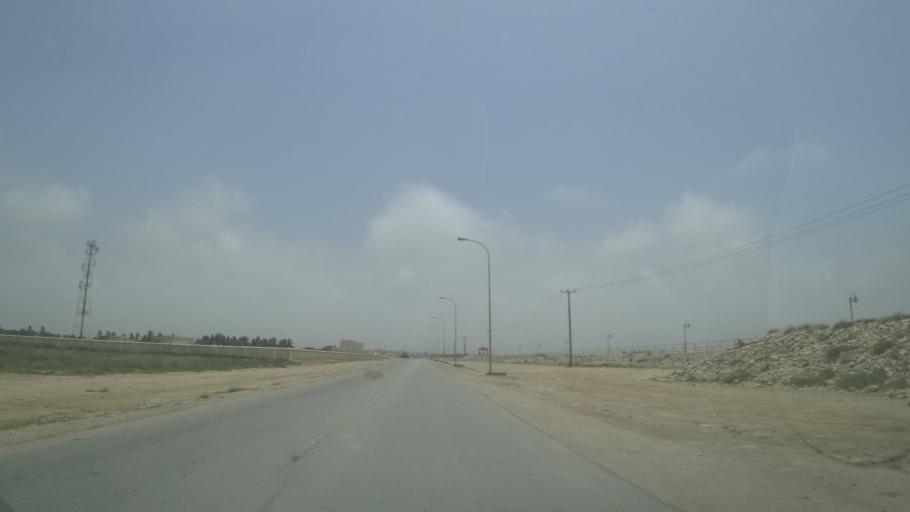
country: OM
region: Zufar
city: Salalah
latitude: 17.0177
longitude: 54.1745
